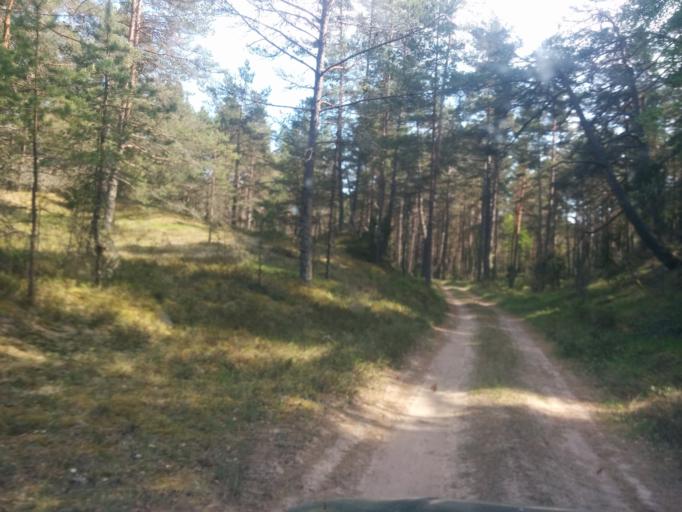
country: LV
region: Dundaga
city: Dundaga
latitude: 57.6212
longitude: 22.0818
